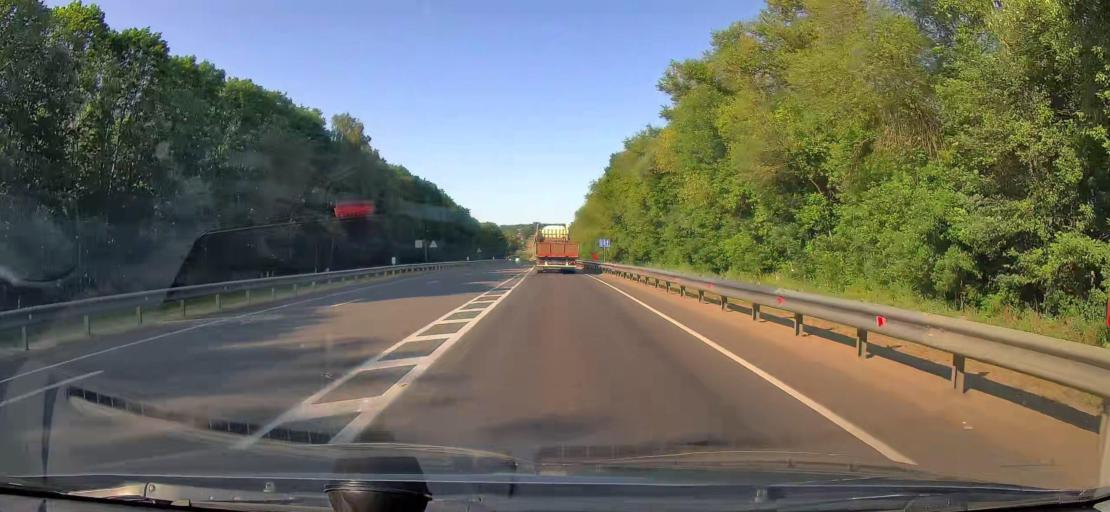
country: RU
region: Orjol
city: Mtsensk
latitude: 53.1920
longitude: 36.4259
